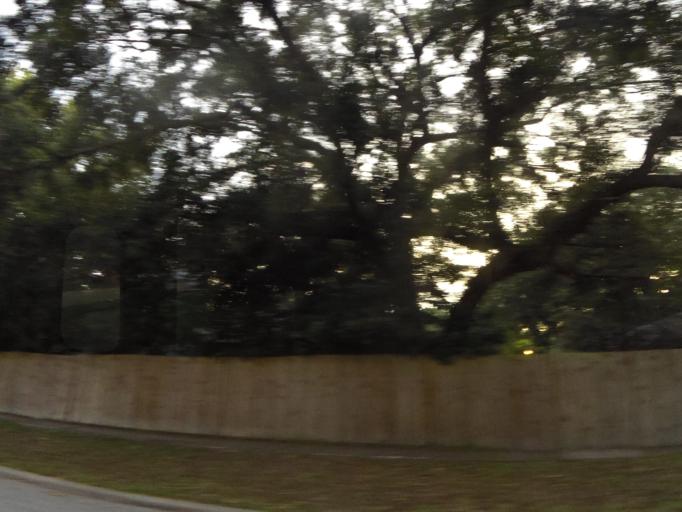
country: US
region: Florida
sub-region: Duval County
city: Atlantic Beach
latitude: 30.3543
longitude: -81.4948
